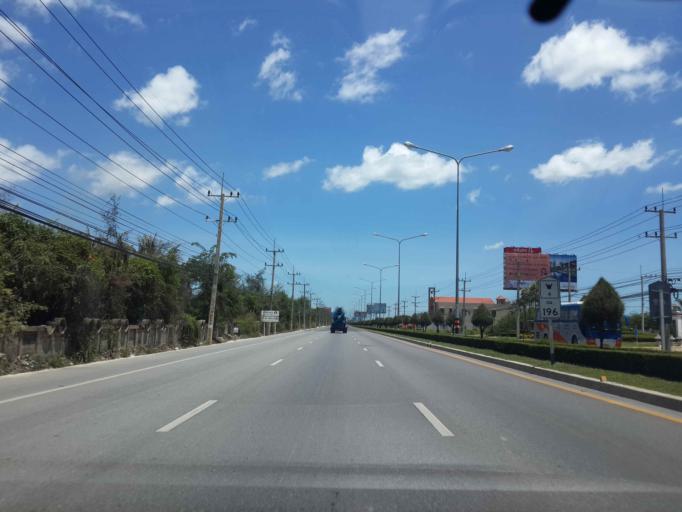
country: TH
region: Phetchaburi
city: Cha-am
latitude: 12.7593
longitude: 99.9631
